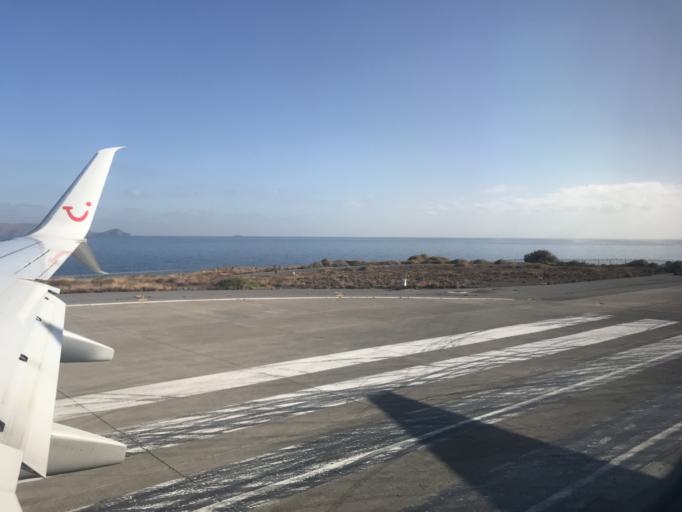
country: GR
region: Crete
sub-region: Nomos Irakleiou
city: Nea Alikarnassos
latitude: 35.3391
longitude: 25.1906
